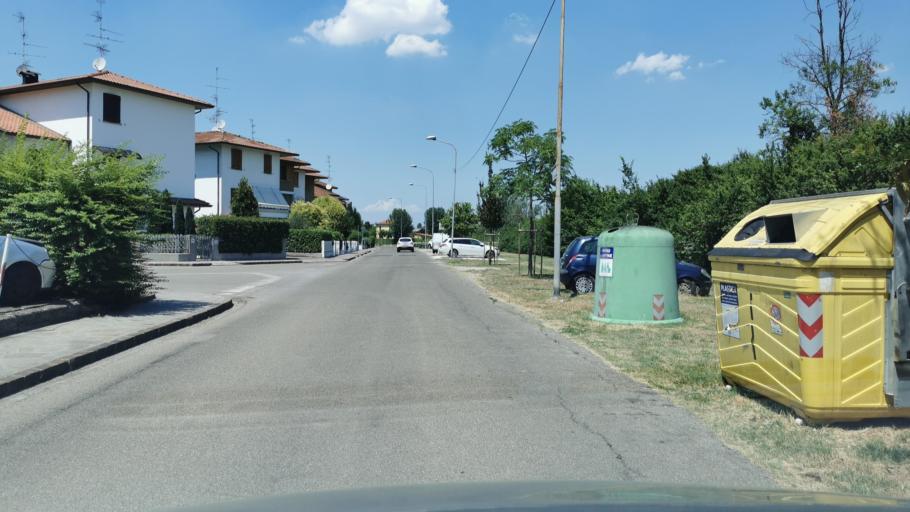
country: IT
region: Emilia-Romagna
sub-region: Provincia di Modena
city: Fossoli
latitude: 44.8021
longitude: 10.8872
